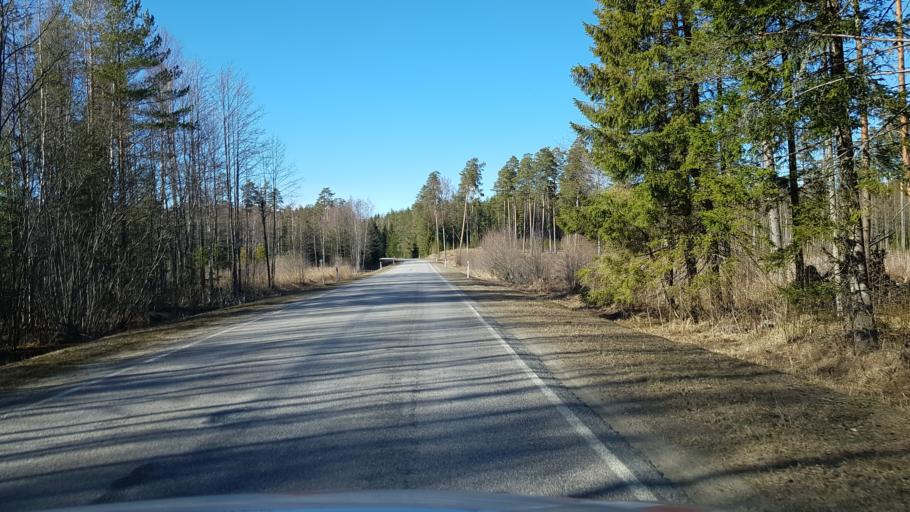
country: EE
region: Laeaene-Virumaa
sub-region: Vinni vald
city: Vinni
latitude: 59.2524
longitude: 26.6878
